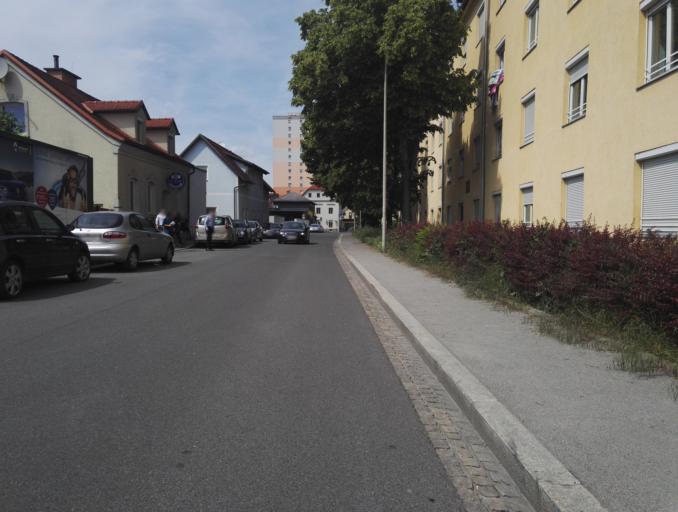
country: AT
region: Styria
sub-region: Graz Stadt
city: Wetzelsdorf
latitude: 47.0528
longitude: 15.4263
